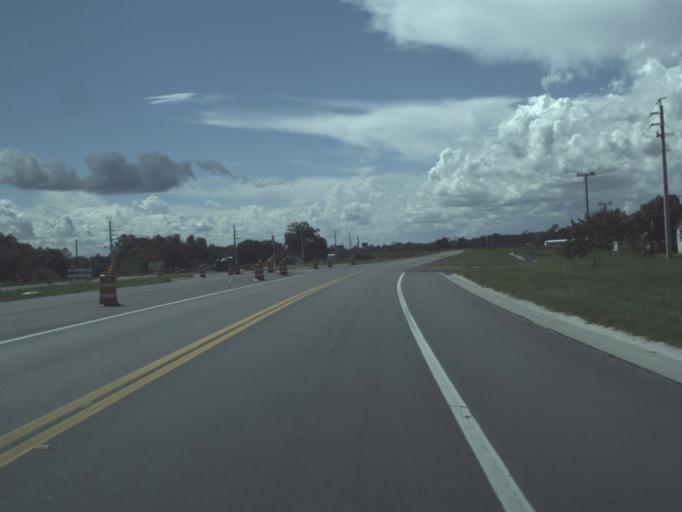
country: US
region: Florida
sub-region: Okeechobee County
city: Taylor Creek
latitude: 27.2579
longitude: -80.7522
